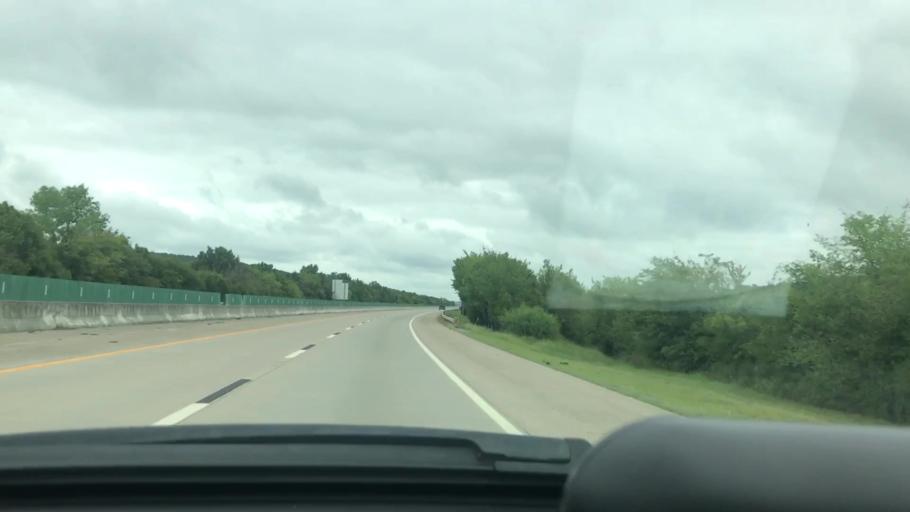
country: US
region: Oklahoma
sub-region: Pittsburg County
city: Krebs
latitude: 35.0151
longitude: -95.7185
